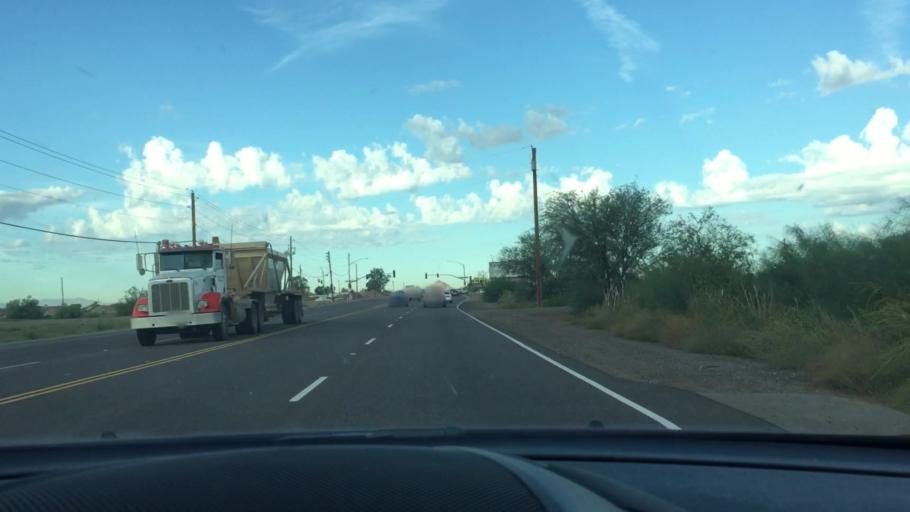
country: US
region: Arizona
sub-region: Maricopa County
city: Mesa
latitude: 33.4634
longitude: -111.8520
